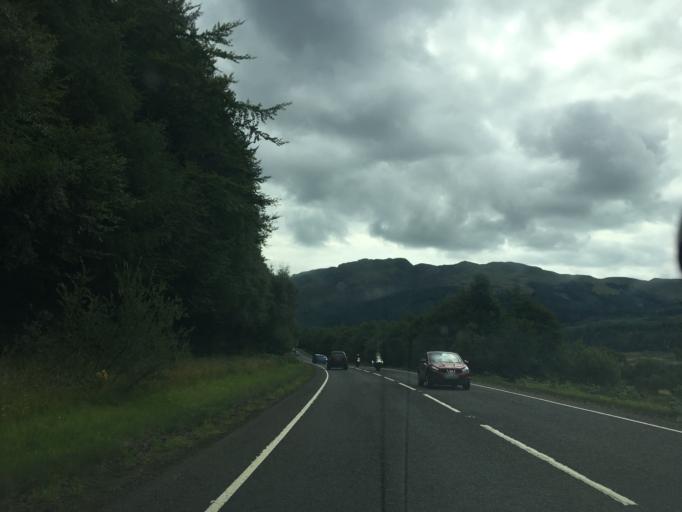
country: GB
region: Scotland
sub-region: Stirling
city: Callander
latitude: 56.3145
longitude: -4.3287
